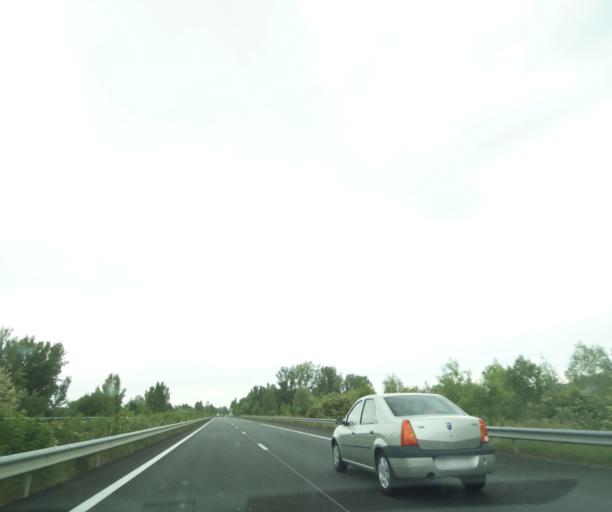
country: FR
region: Midi-Pyrenees
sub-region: Departement du Tarn-et-Garonne
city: Realville
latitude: 44.1214
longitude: 1.4764
